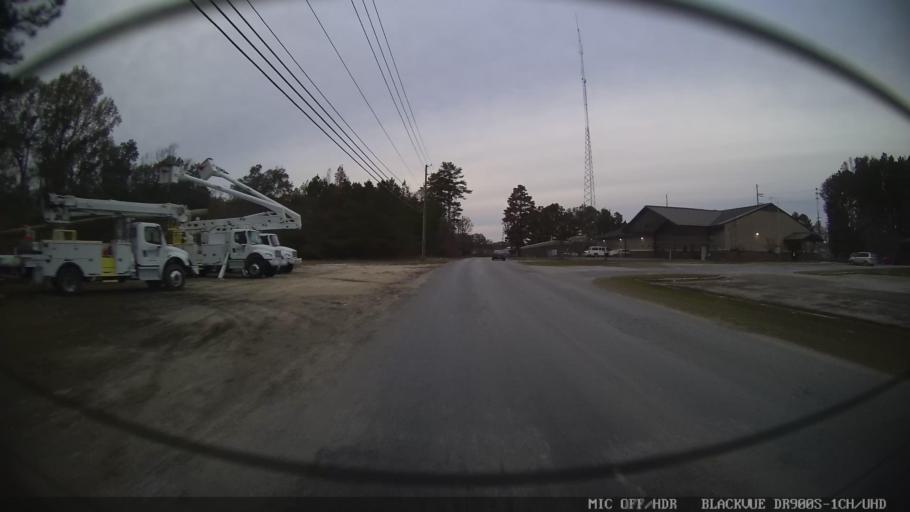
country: US
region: Mississippi
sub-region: Clarke County
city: Quitman
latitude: 32.0407
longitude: -88.7345
